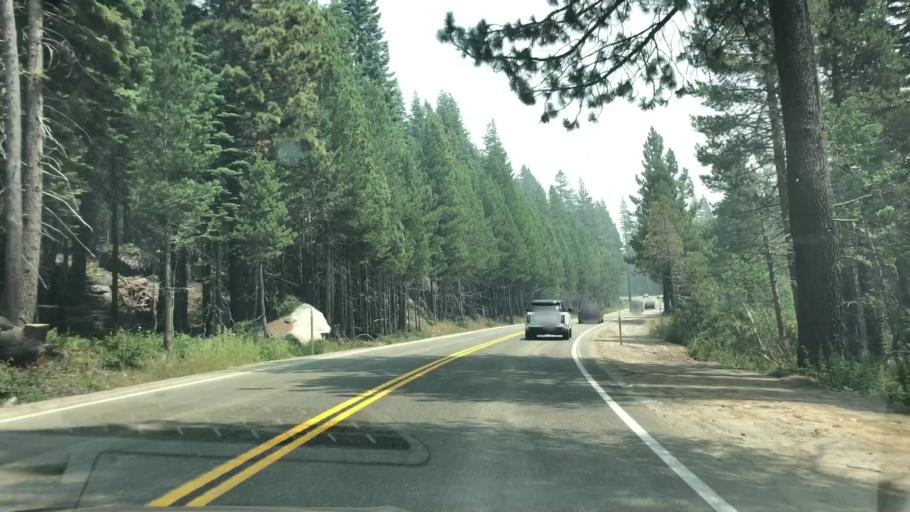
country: US
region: California
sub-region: El Dorado County
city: South Lake Tahoe
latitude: 38.8124
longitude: -120.0899
